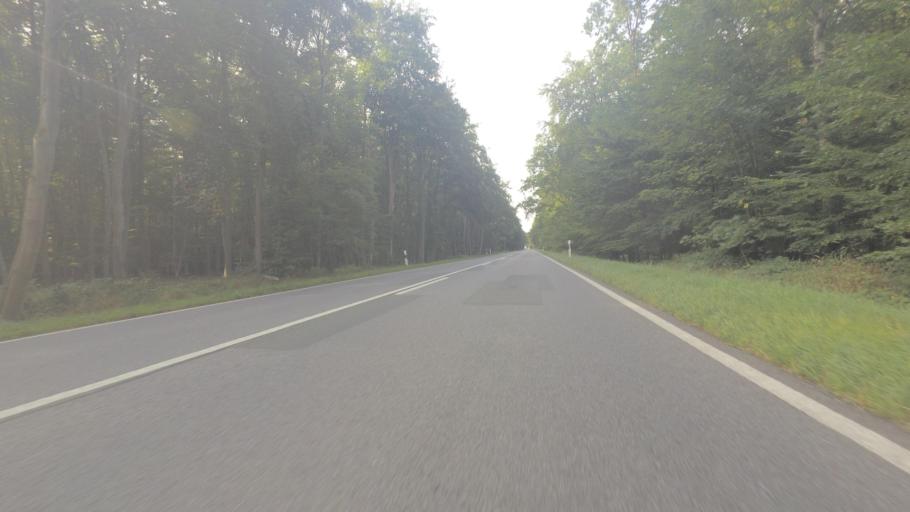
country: DE
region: Mecklenburg-Vorpommern
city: Borrentin
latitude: 53.7550
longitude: 12.9321
